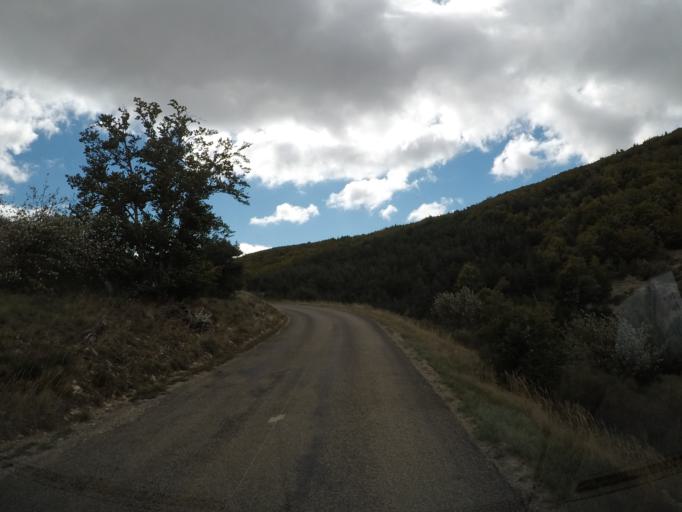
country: FR
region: Provence-Alpes-Cote d'Azur
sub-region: Departement du Vaucluse
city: Sault
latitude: 44.1656
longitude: 5.4962
